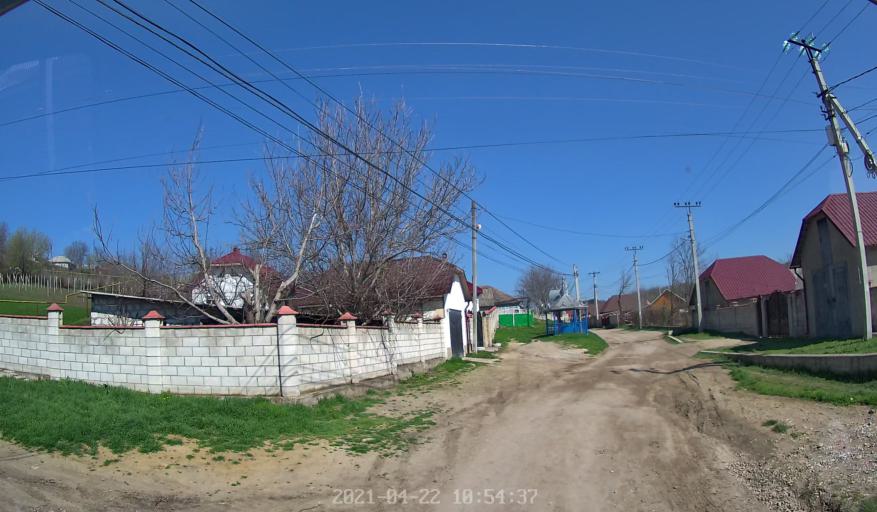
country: MD
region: Chisinau
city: Ciorescu
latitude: 47.1694
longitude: 28.9496
